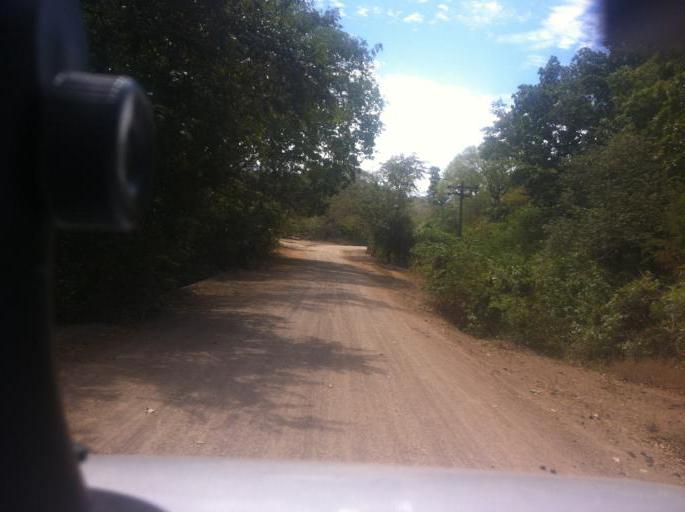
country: NI
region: Granada
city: Nandaime
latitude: 11.6106
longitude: -86.0347
